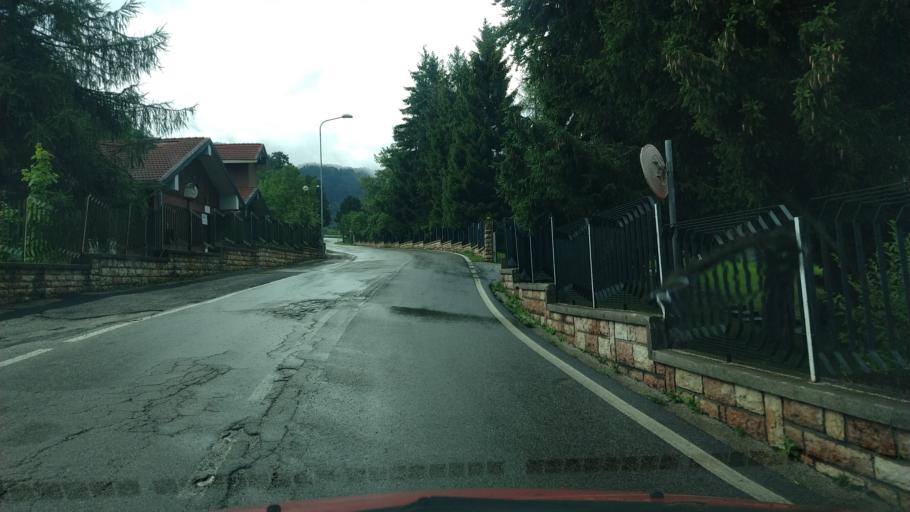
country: IT
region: Veneto
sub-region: Provincia di Vicenza
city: Tonezza del Cimone
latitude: 45.8587
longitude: 11.3373
